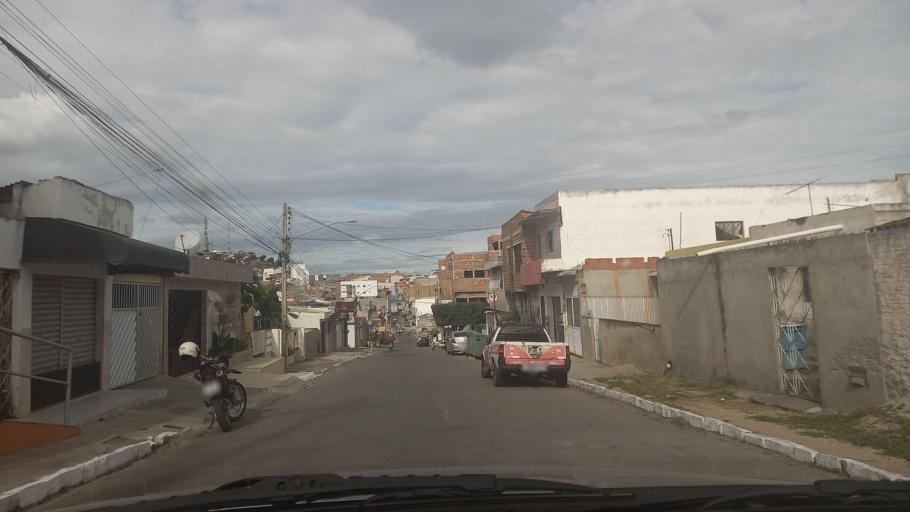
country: BR
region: Pernambuco
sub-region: Caruaru
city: Caruaru
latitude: -8.2851
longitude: -35.9899
